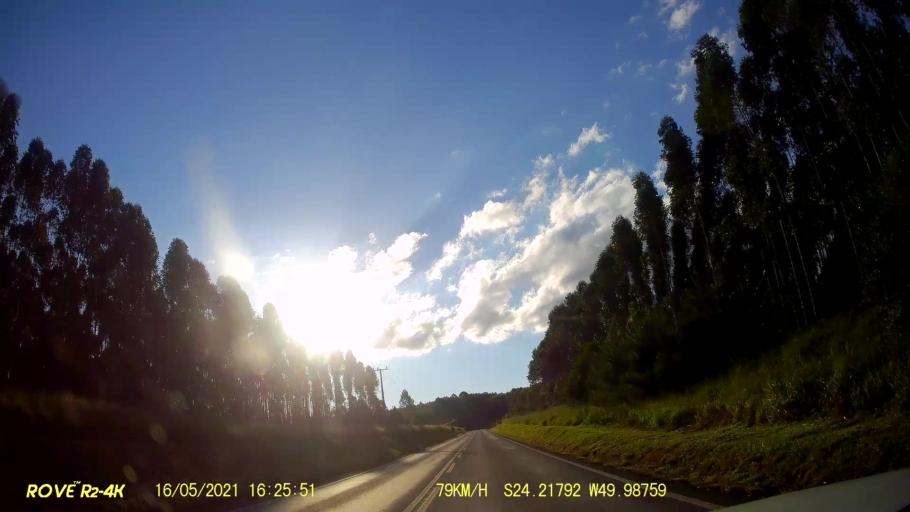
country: BR
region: Parana
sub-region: Jaguariaiva
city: Jaguariaiva
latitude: -24.2178
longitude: -49.9875
